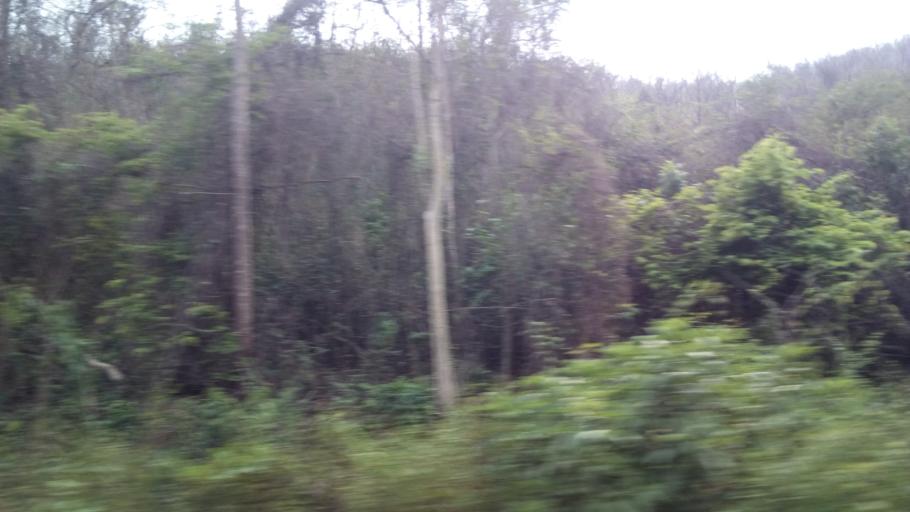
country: TH
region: Sara Buri
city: Saraburi
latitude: 14.4470
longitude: 100.9558
